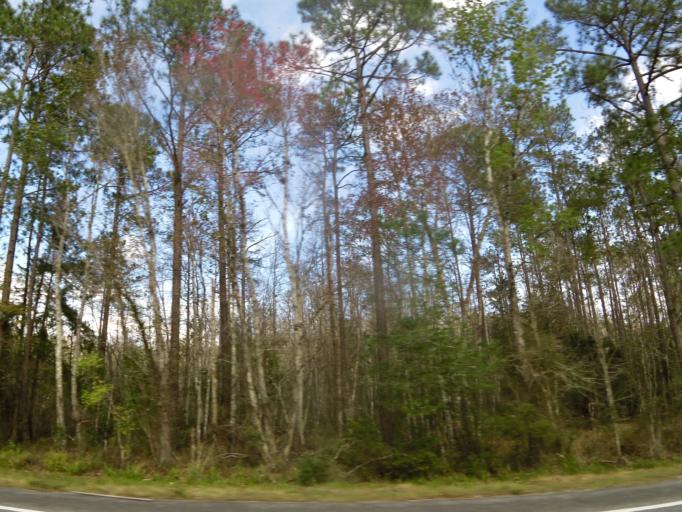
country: US
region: Florida
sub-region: Volusia County
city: Pierson
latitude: 29.2560
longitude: -81.3284
